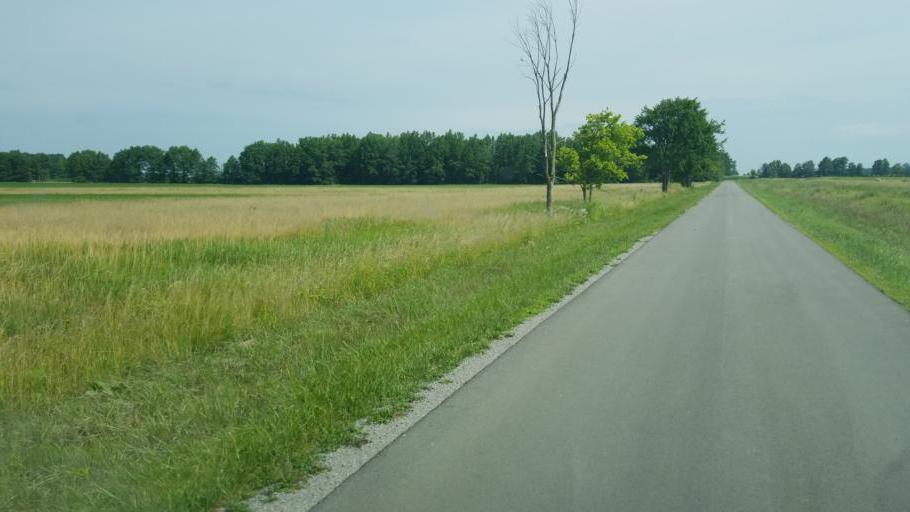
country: US
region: Ohio
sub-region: Wyandot County
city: Upper Sandusky
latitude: 40.7246
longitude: -83.3238
